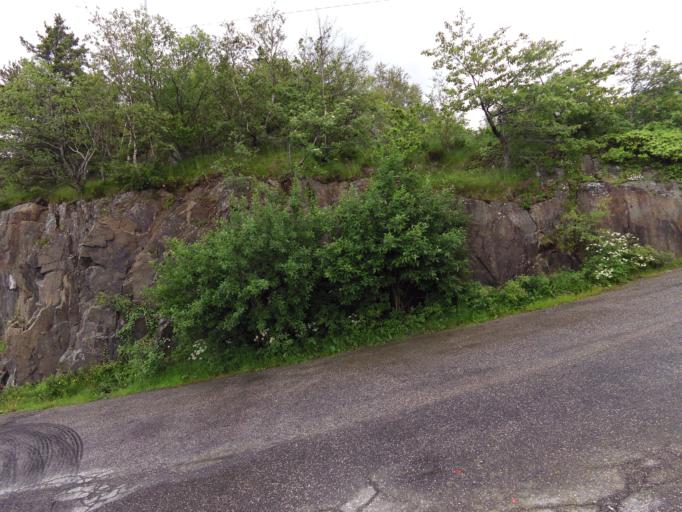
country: NO
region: Vest-Agder
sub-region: Farsund
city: Farsund
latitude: 58.0966
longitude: 6.8144
